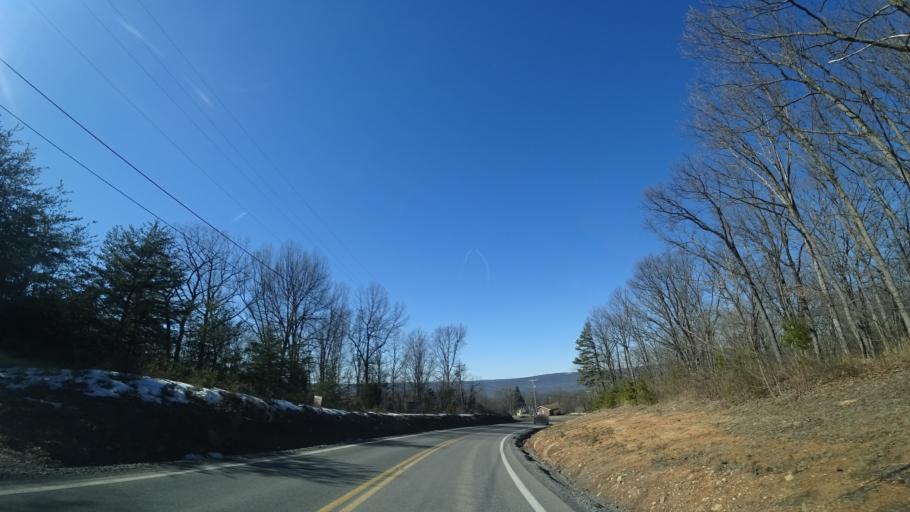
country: US
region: Virginia
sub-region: Shenandoah County
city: Strasburg
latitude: 39.0823
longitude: -78.5311
